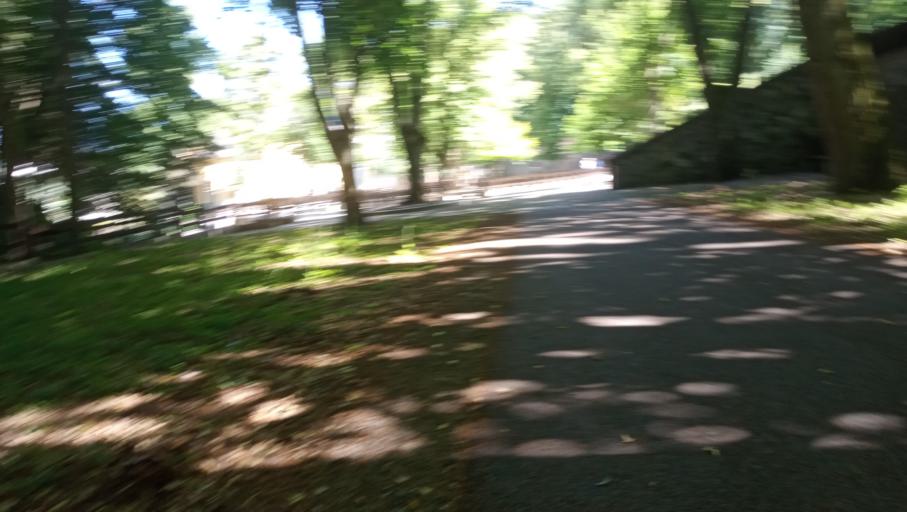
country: HU
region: Nograd
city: Matraverebely
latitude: 48.0006
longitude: 19.7601
